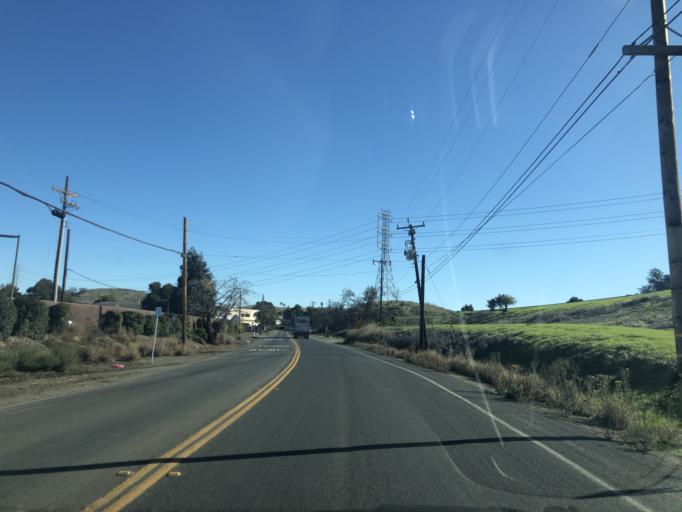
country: US
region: California
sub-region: Contra Costa County
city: Vine Hill
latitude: 38.0059
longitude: -122.0893
